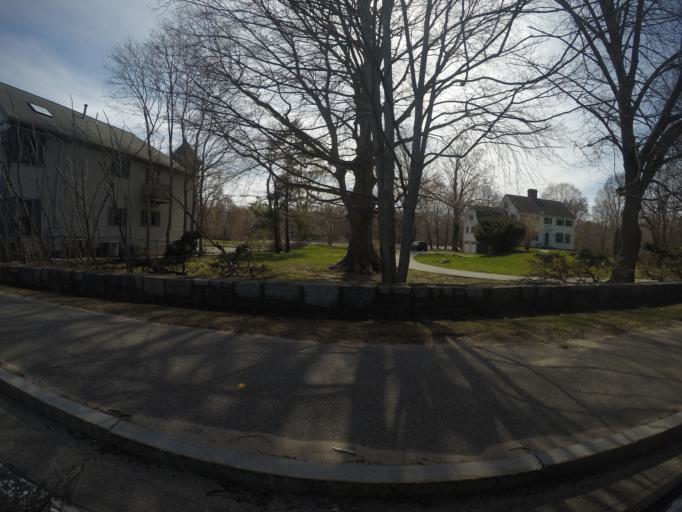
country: US
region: Massachusetts
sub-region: Bristol County
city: Easton
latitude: 42.0482
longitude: -71.0824
